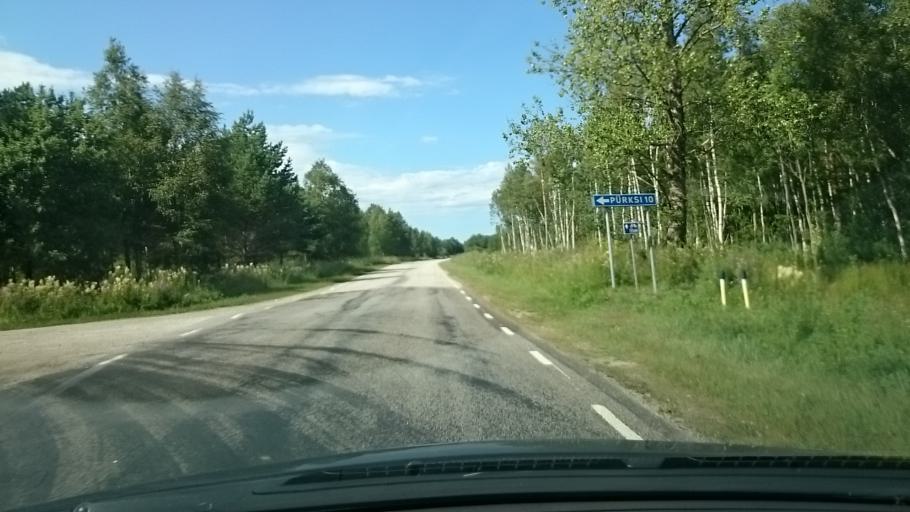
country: EE
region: Laeaene
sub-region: Haapsalu linn
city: Haapsalu
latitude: 59.0883
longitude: 23.5500
